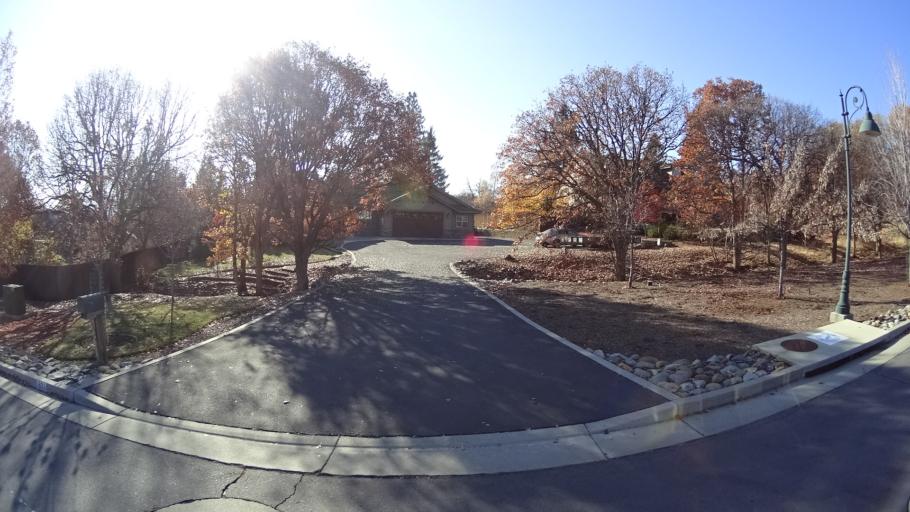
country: US
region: California
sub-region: Siskiyou County
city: Yreka
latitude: 41.7245
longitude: -122.6512
